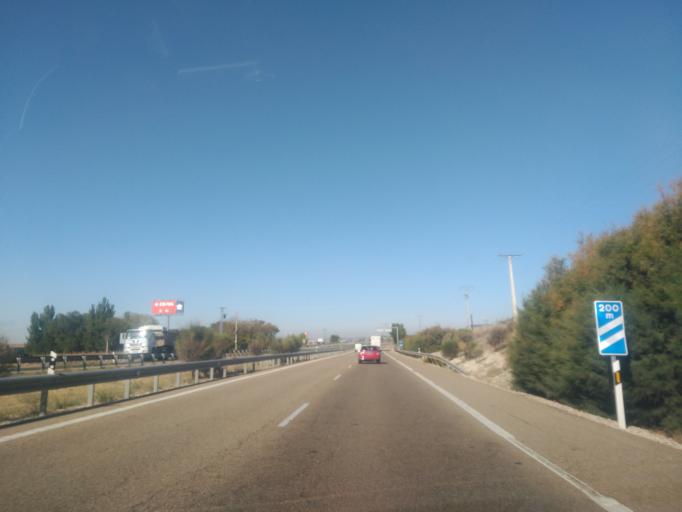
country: ES
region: Castille and Leon
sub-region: Provincia de Valladolid
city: Cisterniga
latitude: 41.5980
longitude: -4.6522
